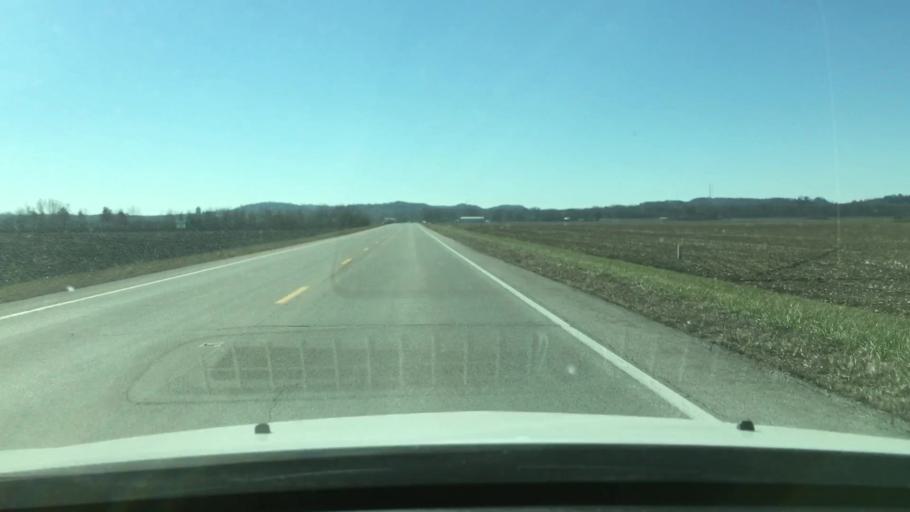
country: US
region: Missouri
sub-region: Pike County
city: Louisiana
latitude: 39.4750
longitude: -91.0216
